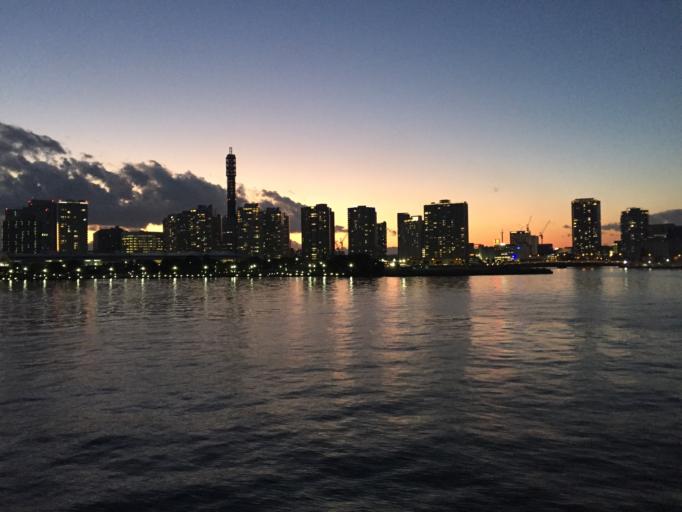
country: JP
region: Kanagawa
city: Yokohama
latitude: 35.4629
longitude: 139.6429
